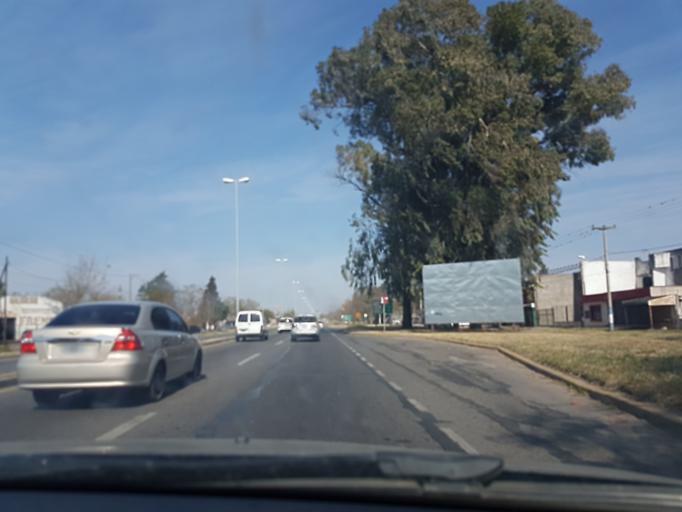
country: AR
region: Cordoba
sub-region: Departamento de Capital
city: Cordoba
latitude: -31.4748
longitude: -64.2337
